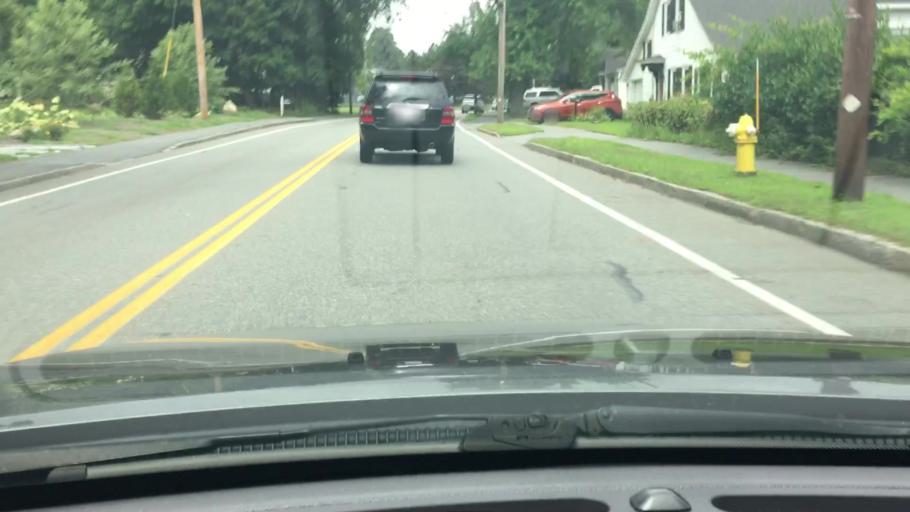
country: US
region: Massachusetts
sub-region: Worcester County
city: Westborough
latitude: 42.2612
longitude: -71.6102
